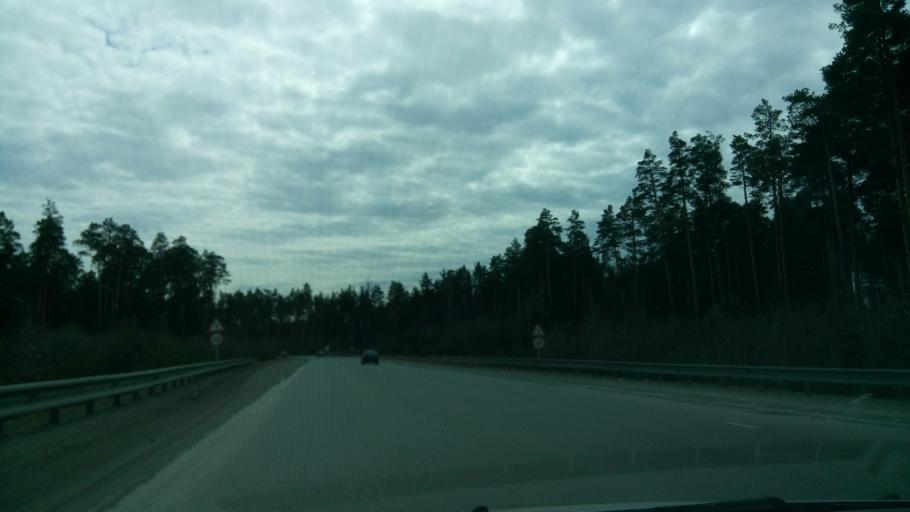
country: RU
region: Sverdlovsk
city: Verkhnyaya Pyshma
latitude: 56.9408
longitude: 60.6329
